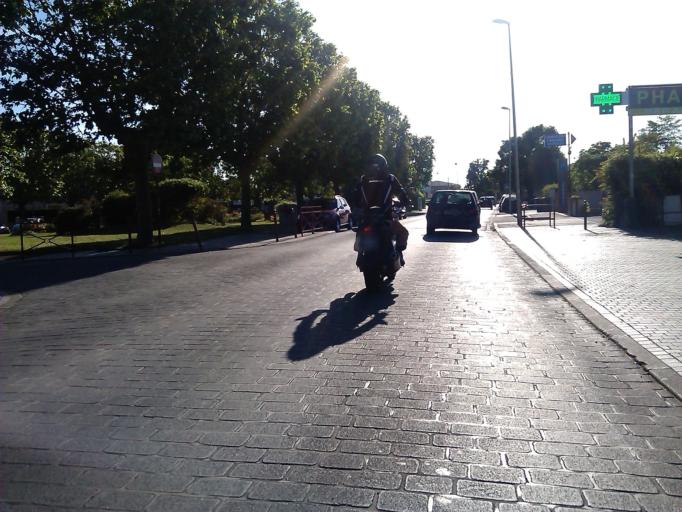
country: FR
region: Aquitaine
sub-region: Departement de la Gironde
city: Pessac
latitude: 44.8023
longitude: -0.6475
